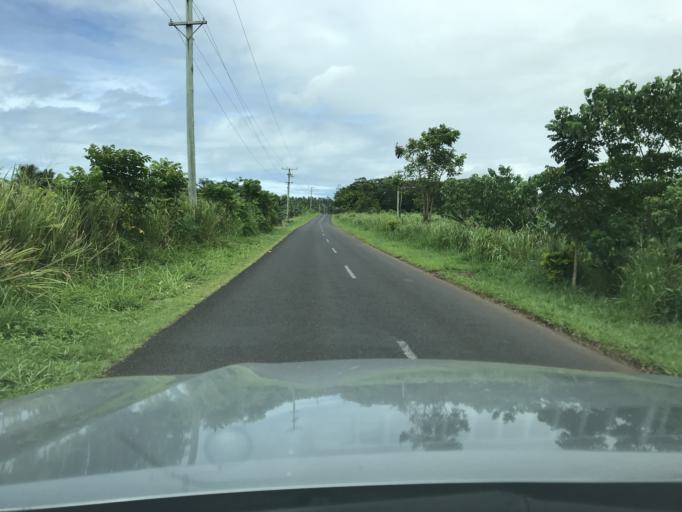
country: WS
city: Nofoali`i
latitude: -13.8742
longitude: -171.9273
